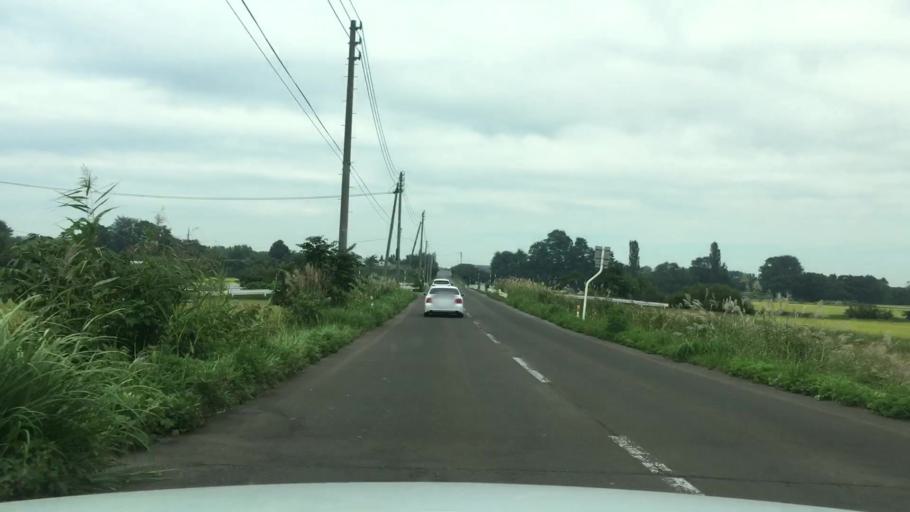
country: JP
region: Aomori
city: Hirosaki
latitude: 40.6495
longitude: 140.4227
